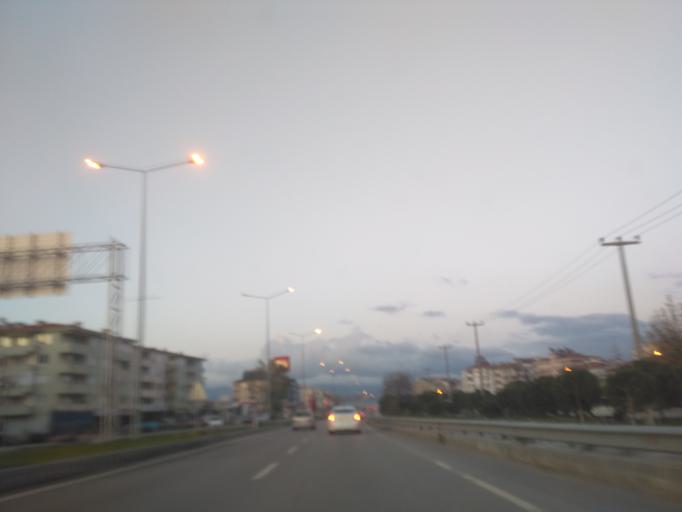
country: TR
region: Balikesir
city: Burhaniye
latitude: 39.5042
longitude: 26.9702
